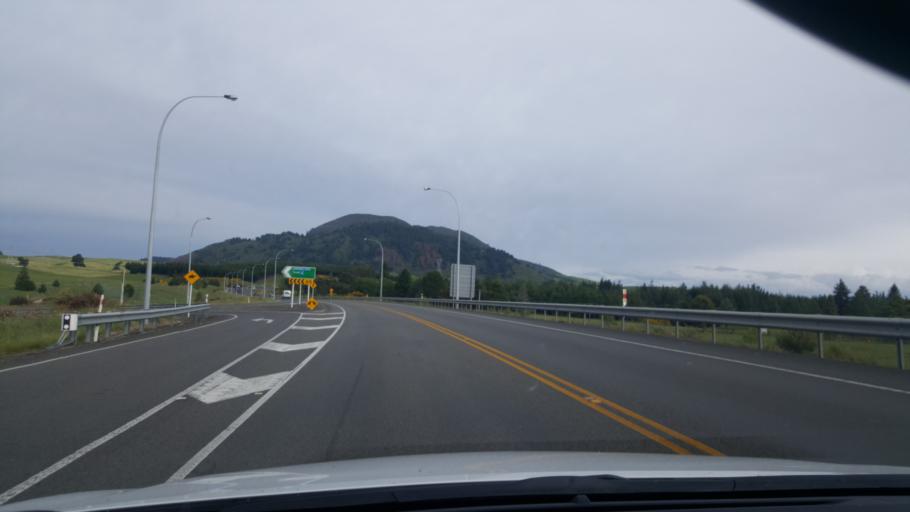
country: NZ
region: Waikato
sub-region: Taupo District
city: Taupo
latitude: -38.6690
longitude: 176.1050
